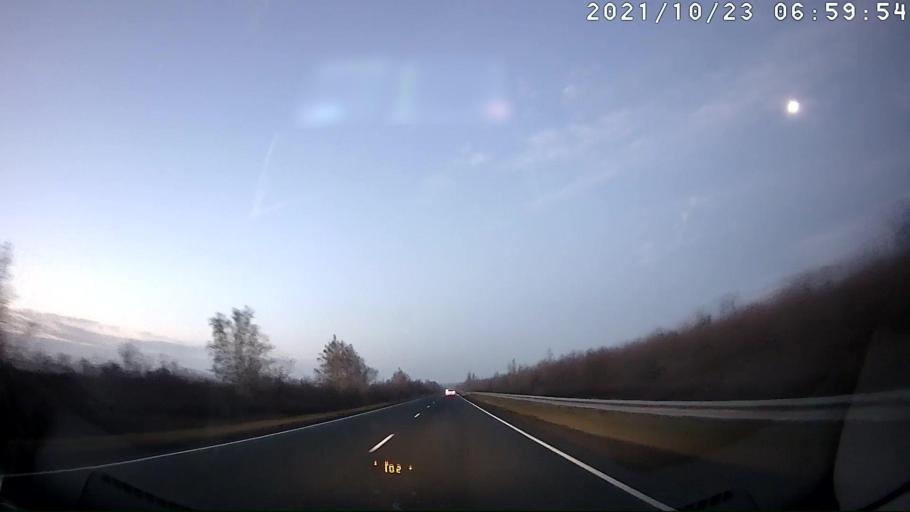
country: RU
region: Saratov
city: Dukhovnitskoye
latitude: 52.6761
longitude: 48.2274
